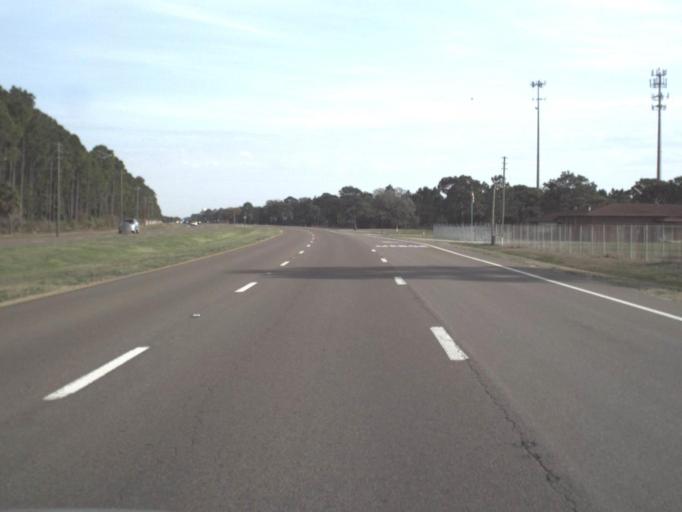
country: US
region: Florida
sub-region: Bay County
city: Tyndall Air Force Base
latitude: 30.0838
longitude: -85.6077
